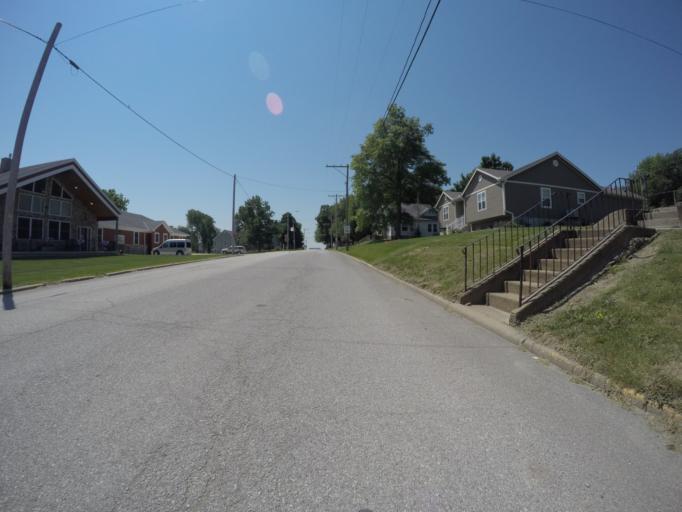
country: US
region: Kansas
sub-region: Doniphan County
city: Highland
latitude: 39.8584
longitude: -95.2652
